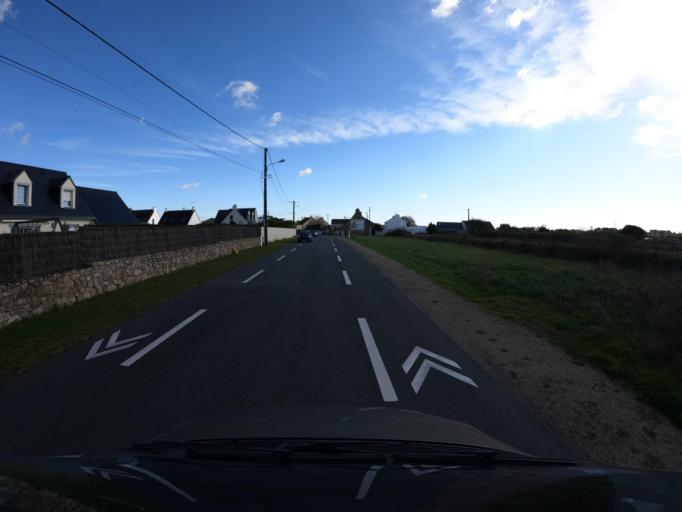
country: FR
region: Pays de la Loire
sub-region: Departement de la Loire-Atlantique
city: Le Pouliguen
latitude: 47.2773
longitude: -2.4487
